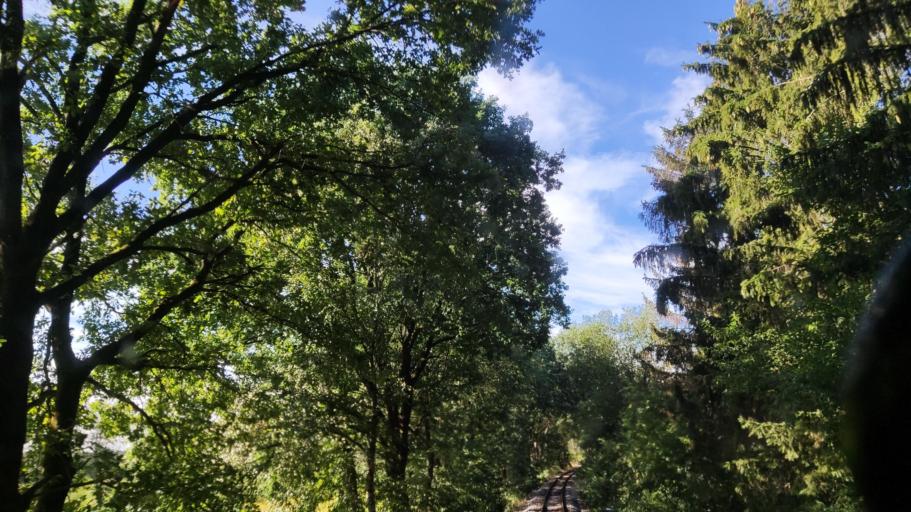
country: DE
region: Lower Saxony
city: Bispingen
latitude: 53.0365
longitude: 9.9353
